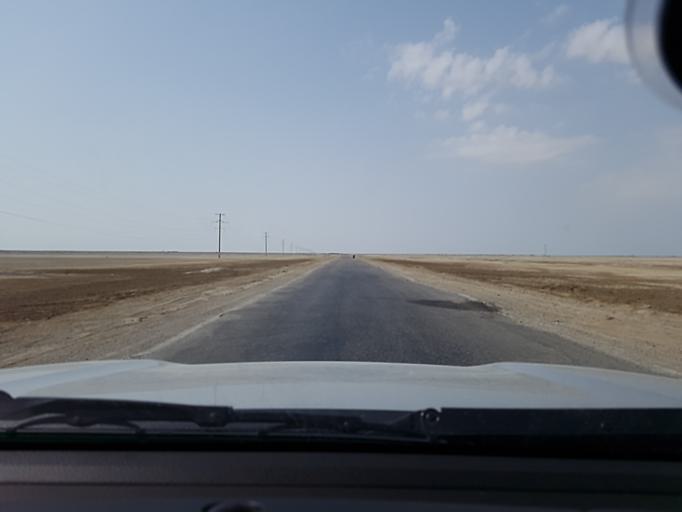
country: TM
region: Balkan
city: Gumdag
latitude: 39.0531
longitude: 54.5843
